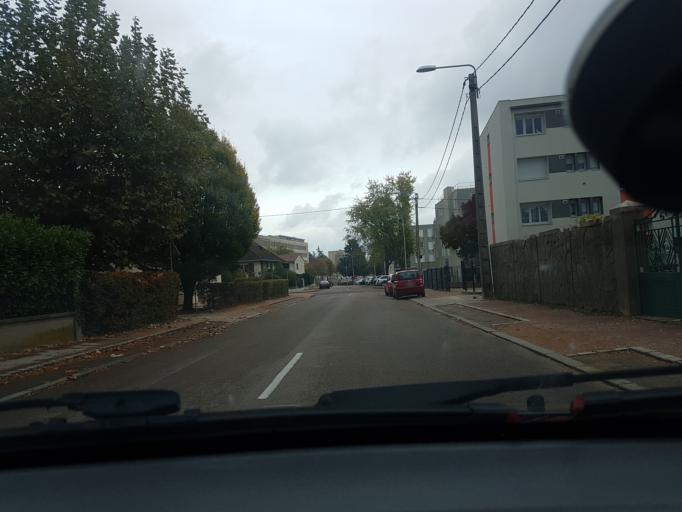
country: FR
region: Bourgogne
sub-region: Departement de la Cote-d'Or
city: Saint-Apollinaire
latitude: 47.3155
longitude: 5.0620
